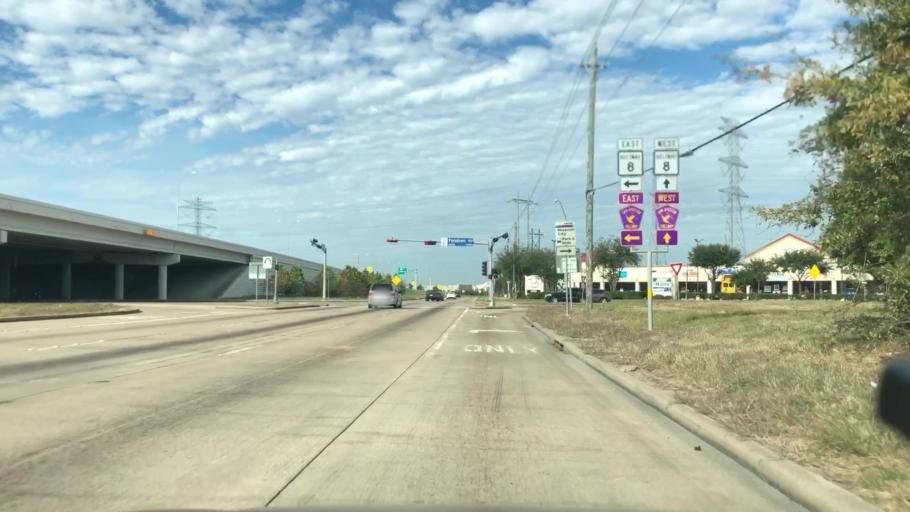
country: US
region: Texas
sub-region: Fort Bend County
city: Missouri City
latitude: 29.6208
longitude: -95.5076
